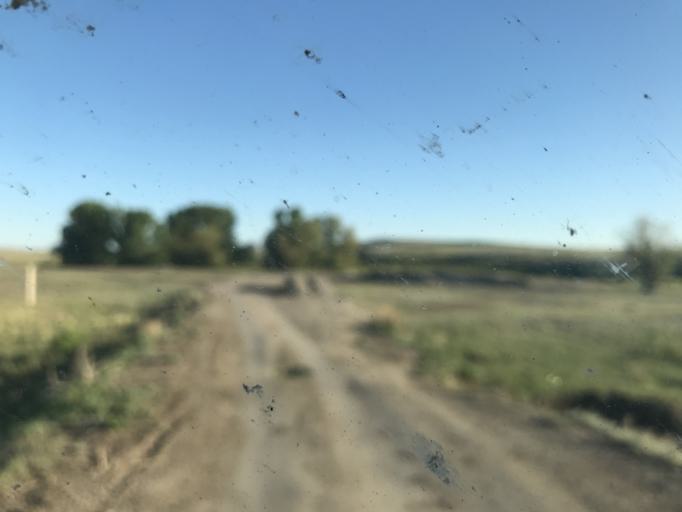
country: KZ
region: Aqtoebe
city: Aqtobe
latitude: 50.2896
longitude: 57.6799
